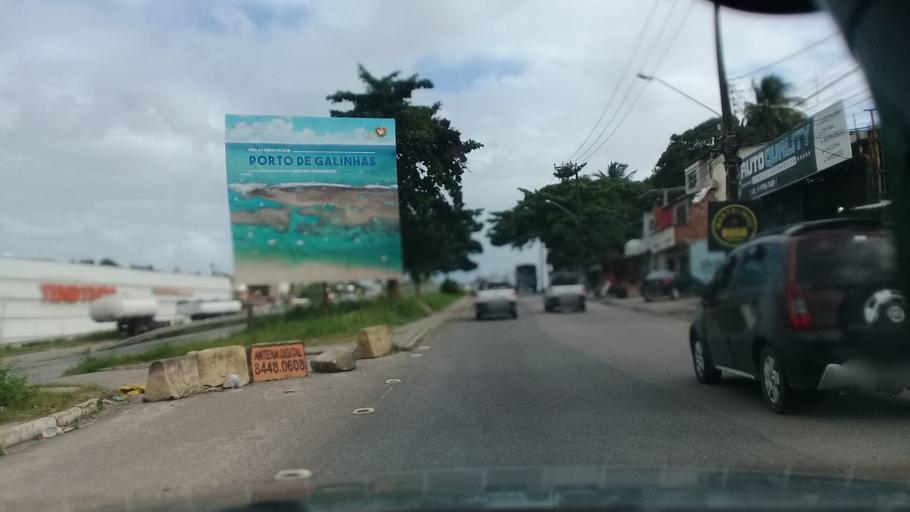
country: BR
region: Pernambuco
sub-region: Olinda
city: Olinda
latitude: -7.9963
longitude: -34.8552
